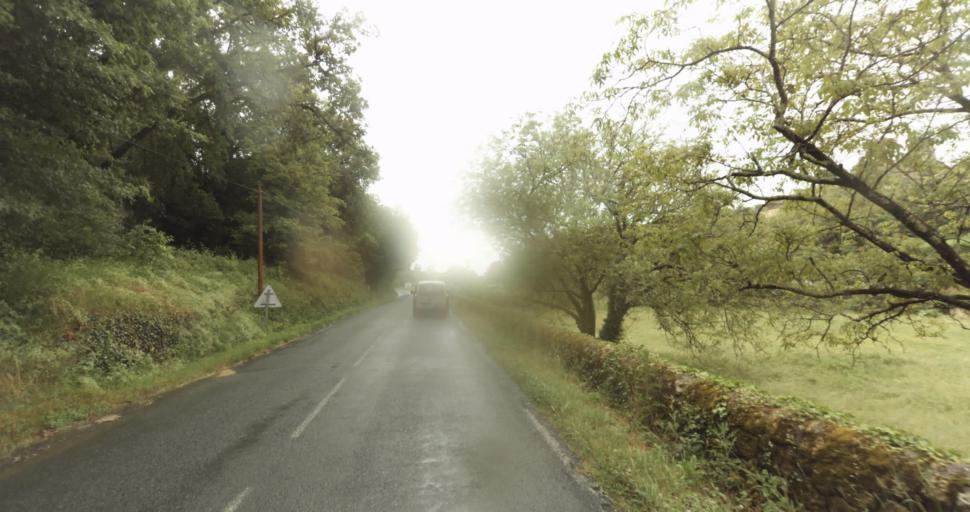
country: FR
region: Aquitaine
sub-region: Departement de la Dordogne
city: Beaumont-du-Perigord
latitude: 44.7741
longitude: 0.8131
